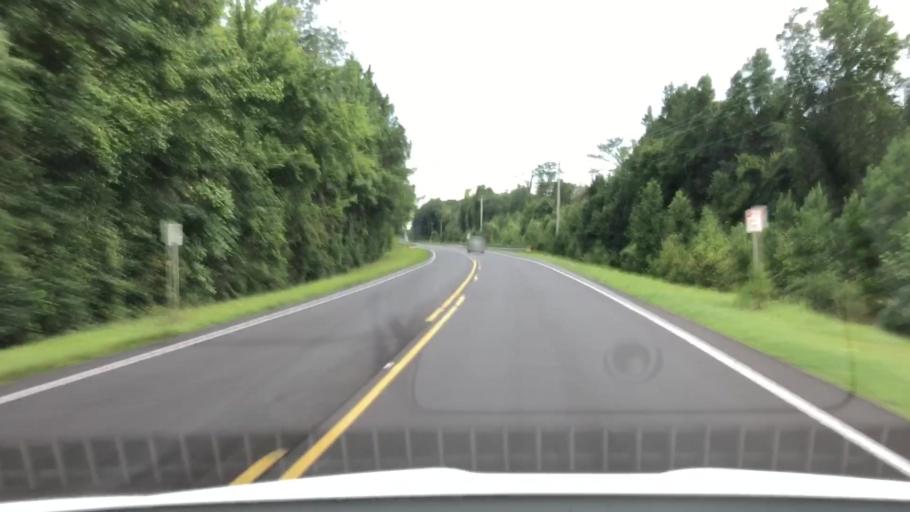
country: US
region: North Carolina
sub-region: Jones County
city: Maysville
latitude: 34.8704
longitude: -77.1951
